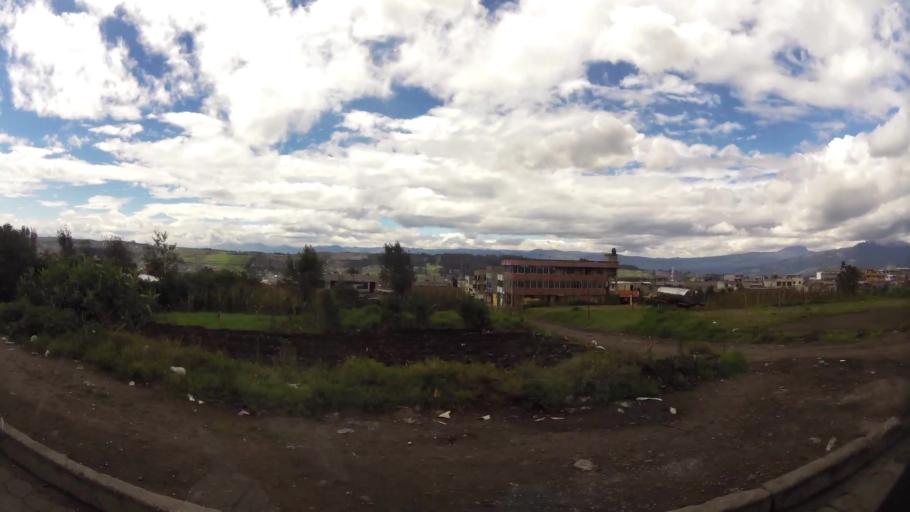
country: EC
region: Pichincha
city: Sangolqui
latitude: -0.3371
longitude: -78.5555
